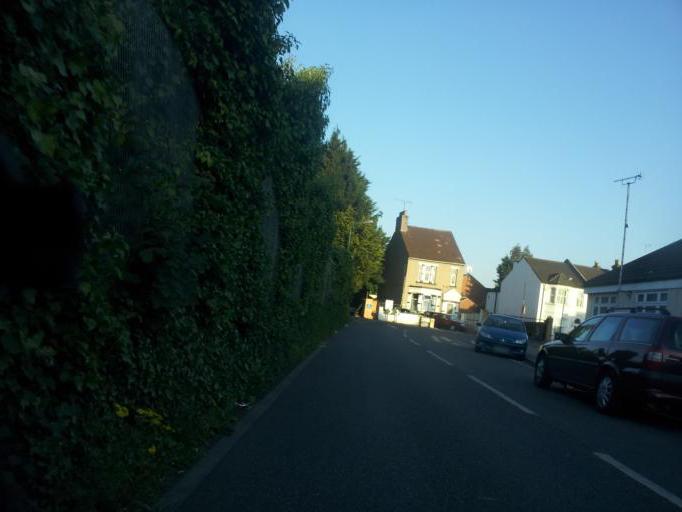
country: GB
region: England
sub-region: Greater London
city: Erith
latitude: 51.4872
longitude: 0.1681
